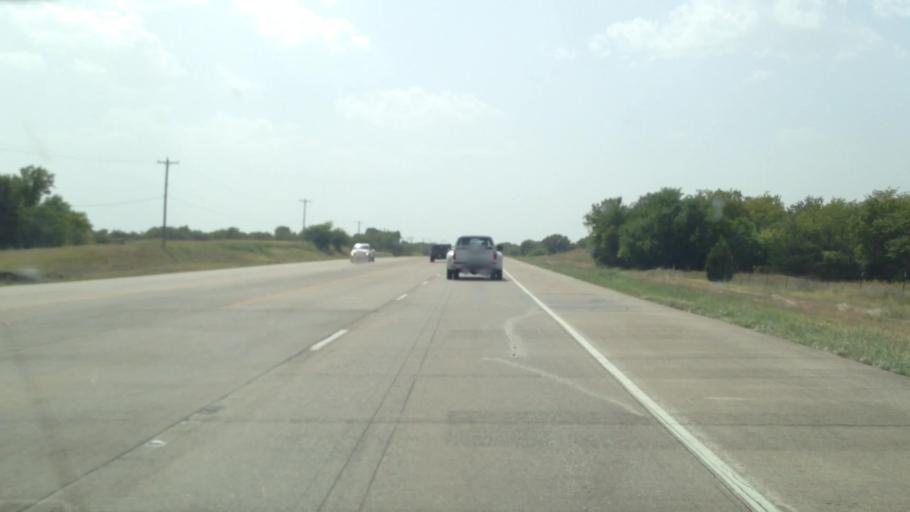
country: US
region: Texas
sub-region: Collin County
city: Princeton
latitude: 33.1695
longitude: -96.4699
